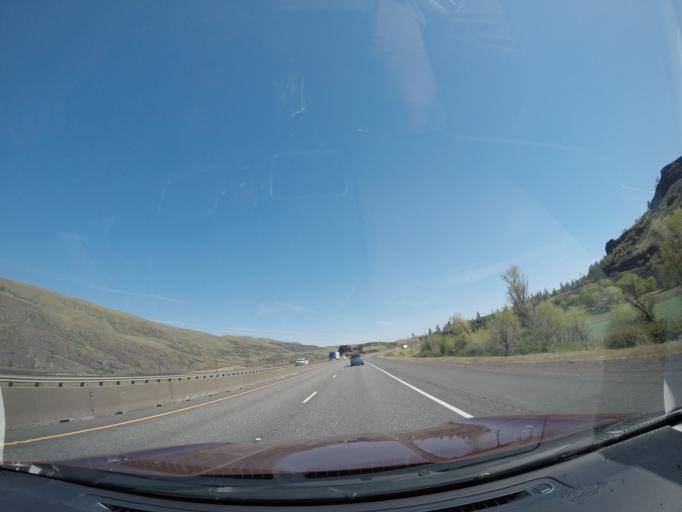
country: US
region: Oregon
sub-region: Wasco County
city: Chenoweth
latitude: 45.6660
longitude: -121.2261
